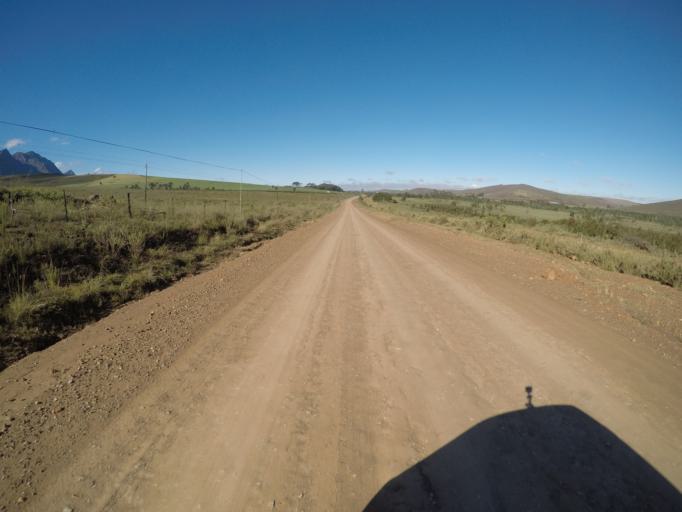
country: ZA
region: Western Cape
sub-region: Overberg District Municipality
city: Caledon
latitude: -34.0628
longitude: 19.6253
